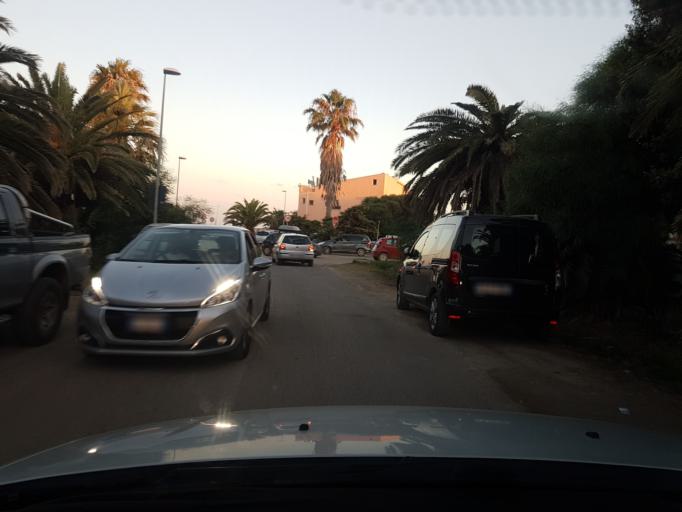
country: IT
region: Sardinia
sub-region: Provincia di Oristano
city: Riola Sardo
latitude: 40.0340
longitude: 8.3994
